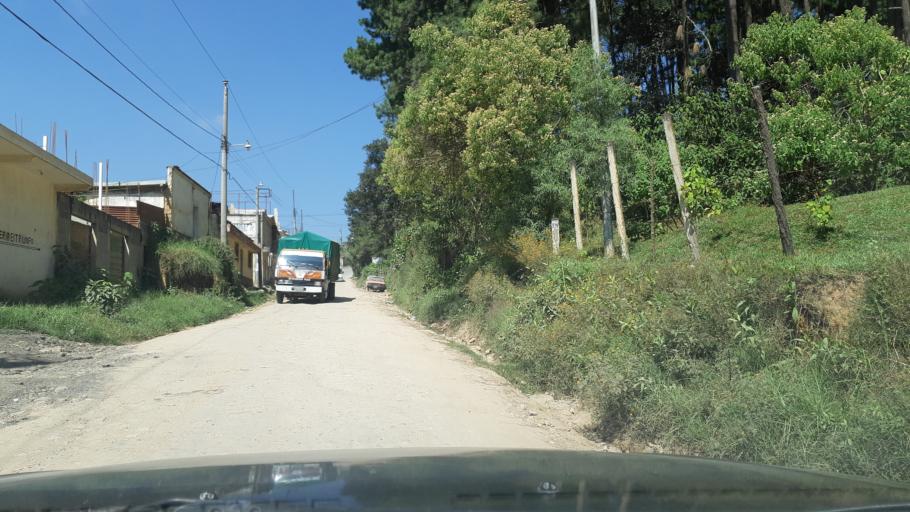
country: GT
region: Chimaltenango
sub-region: Municipio de Chimaltenango
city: Chimaltenango
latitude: 14.6709
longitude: -90.8390
